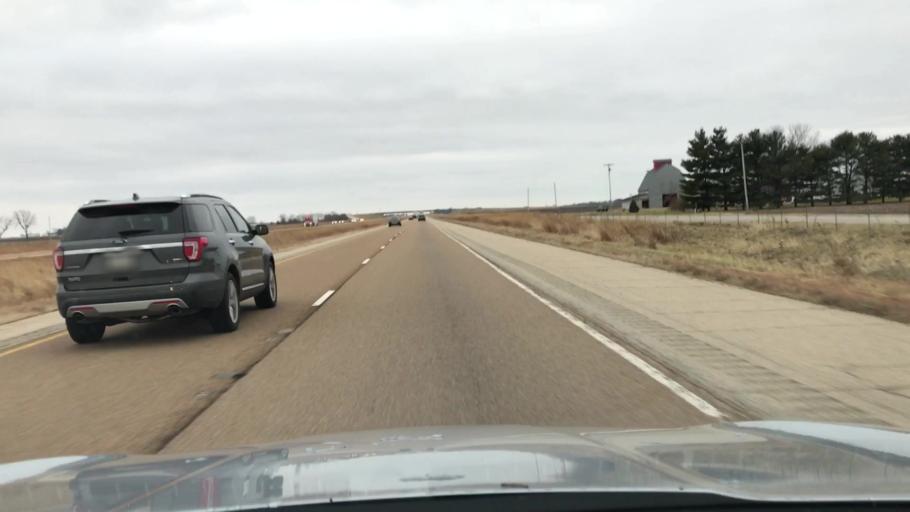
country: US
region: Illinois
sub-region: Montgomery County
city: Raymond
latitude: 39.3886
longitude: -89.6433
